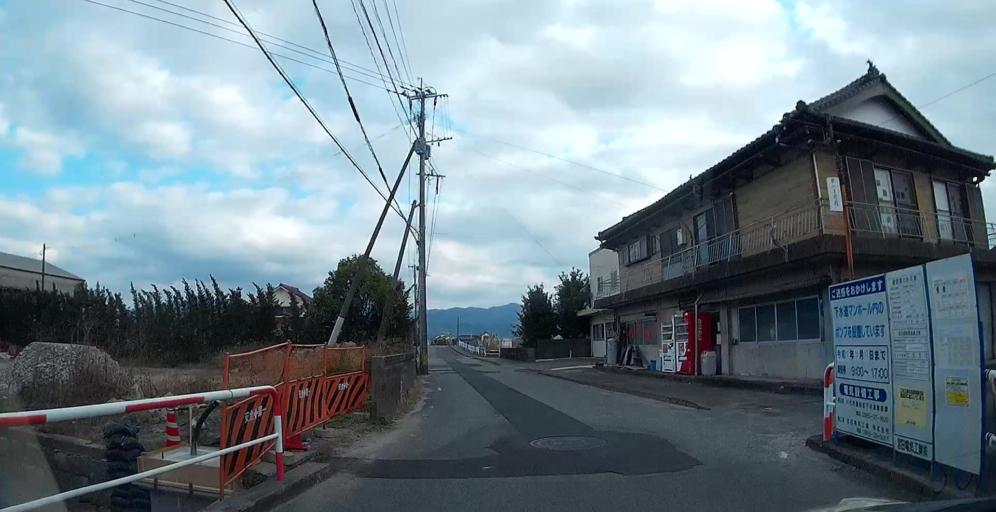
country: JP
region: Kumamoto
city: Yatsushiro
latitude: 32.5480
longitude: 130.6154
